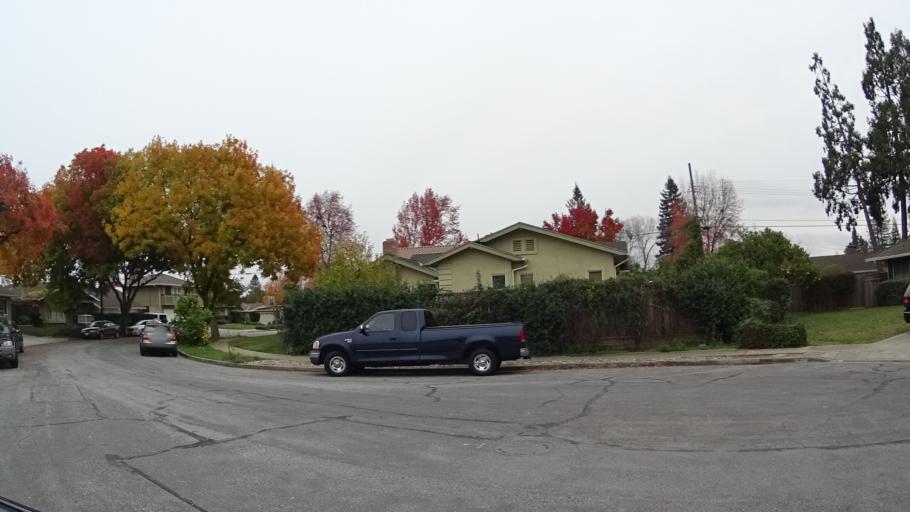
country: US
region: California
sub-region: Santa Clara County
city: Sunnyvale
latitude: 37.3554
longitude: -122.0561
